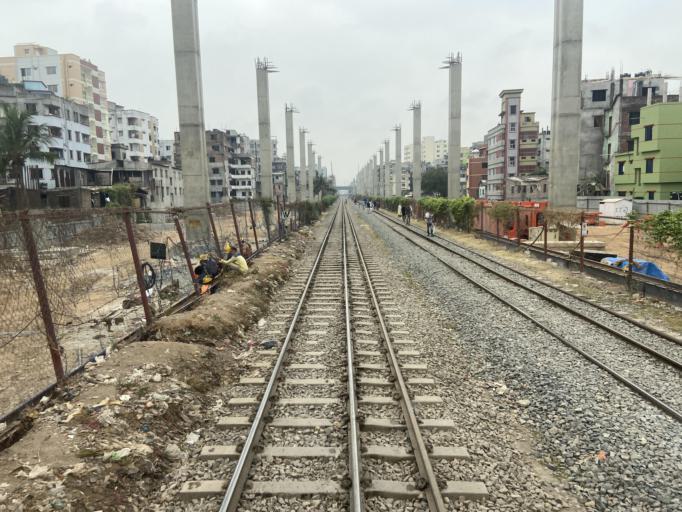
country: BD
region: Dhaka
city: Paltan
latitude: 23.7725
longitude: 90.3968
